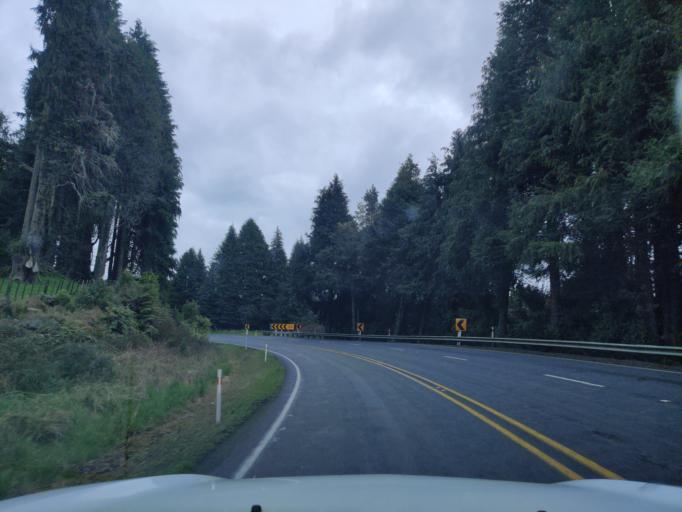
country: NZ
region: Waikato
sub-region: Otorohanga District
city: Otorohanga
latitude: -38.4993
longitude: 175.2007
